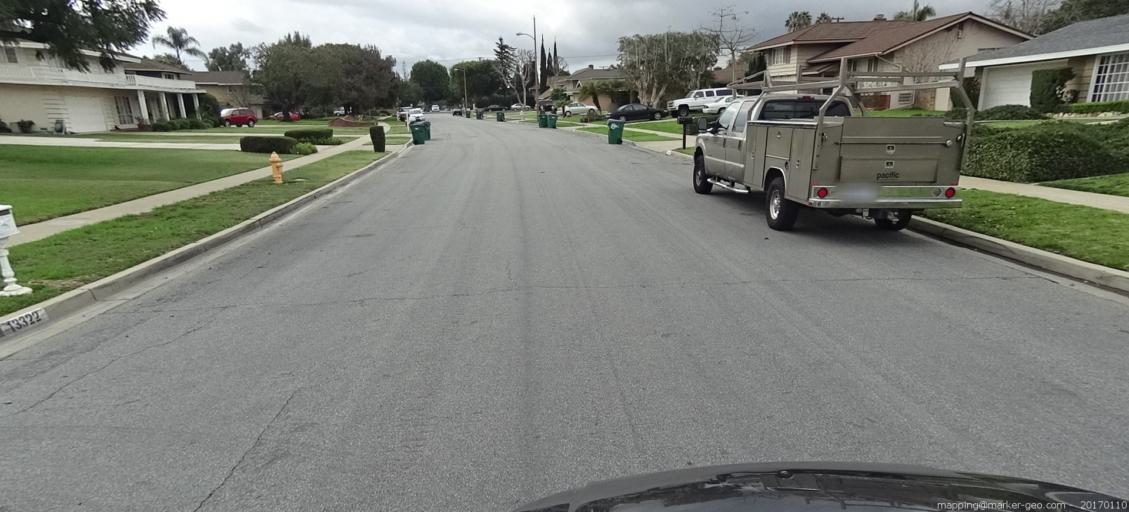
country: US
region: California
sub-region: Orange County
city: Tustin
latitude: 33.7690
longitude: -117.8233
